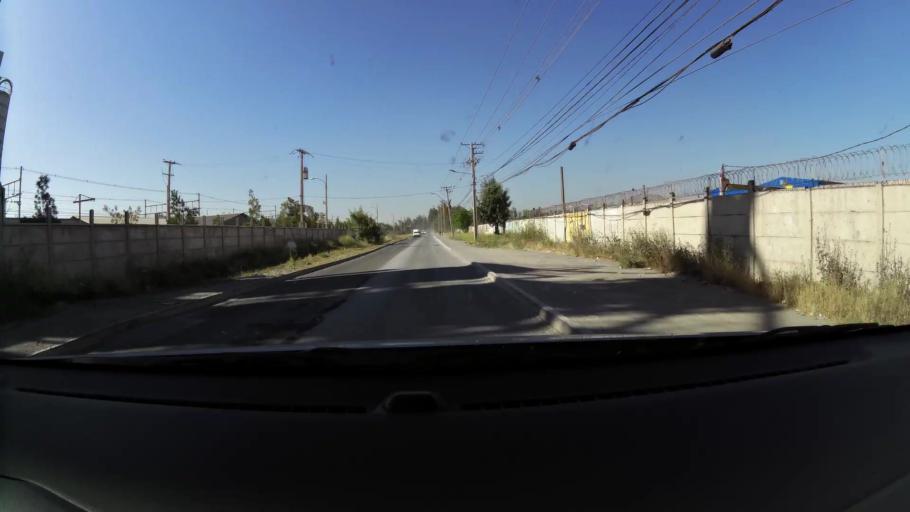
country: CL
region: Santiago Metropolitan
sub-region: Provincia de Maipo
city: San Bernardo
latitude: -33.5575
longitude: -70.6959
